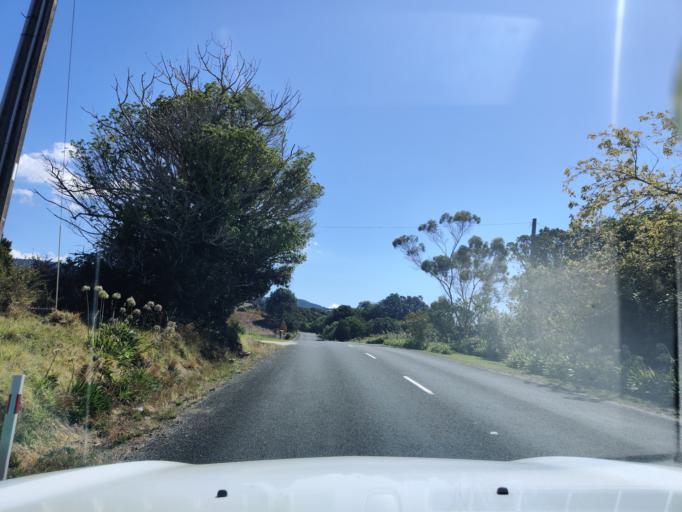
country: NZ
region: Waikato
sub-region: Thames-Coromandel District
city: Thames
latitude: -37.0444
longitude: 175.2976
